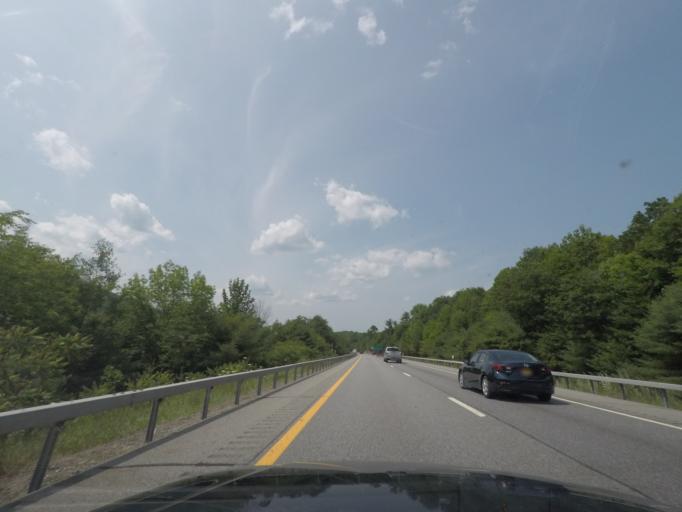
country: US
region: New York
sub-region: Warren County
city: Warrensburg
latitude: 43.4694
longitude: -73.7464
